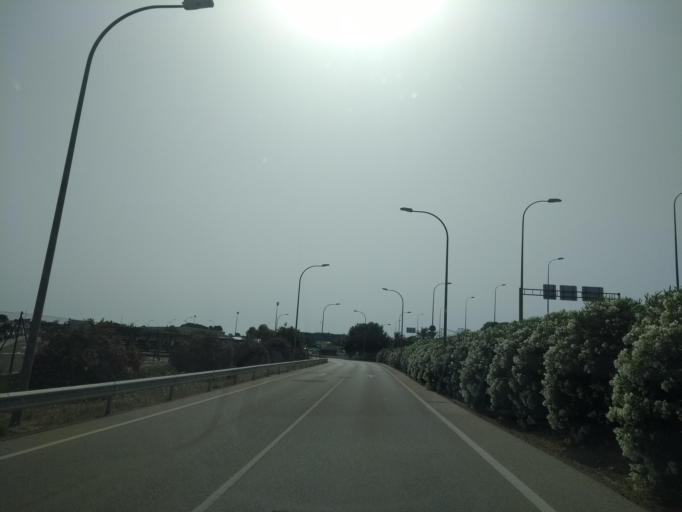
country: ES
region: Balearic Islands
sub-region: Illes Balears
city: s'Arenal
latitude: 39.5442
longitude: 2.7247
